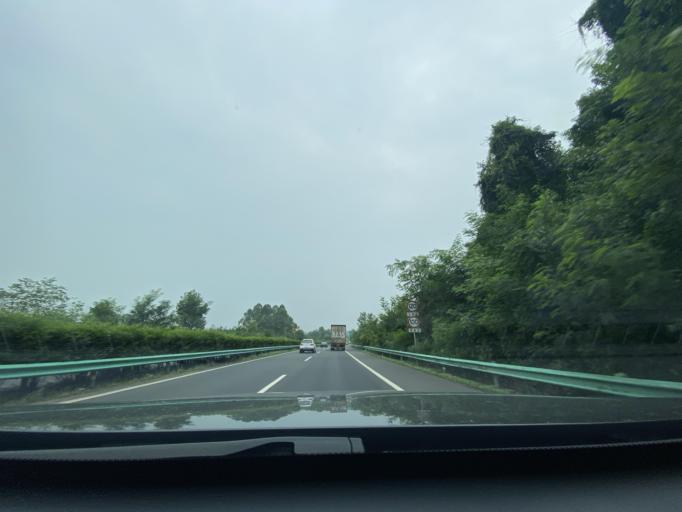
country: CN
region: Sichuan
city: Longquan
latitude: 30.3090
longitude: 104.1185
